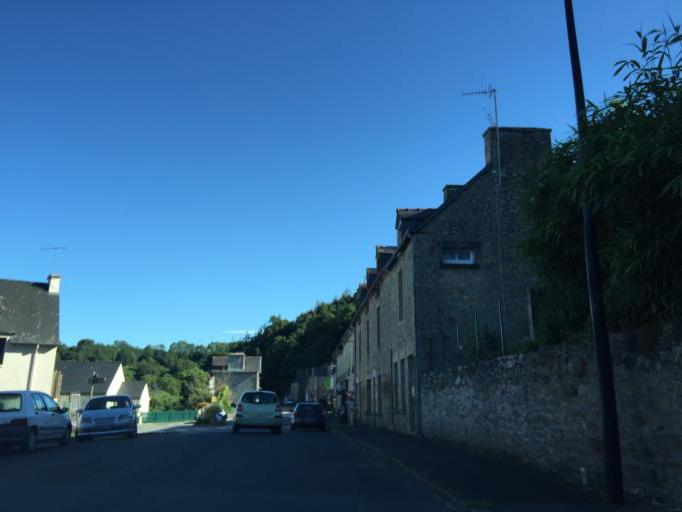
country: FR
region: Brittany
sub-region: Departement des Cotes-d'Armor
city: Jugon-les-Lacs
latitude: 48.4093
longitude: -2.3200
